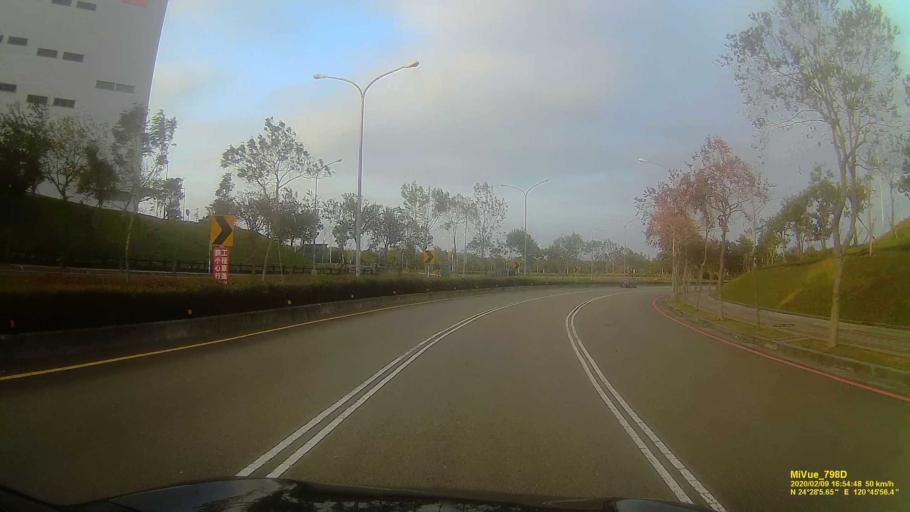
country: TW
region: Taiwan
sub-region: Miaoli
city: Miaoli
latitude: 24.4685
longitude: 120.7656
